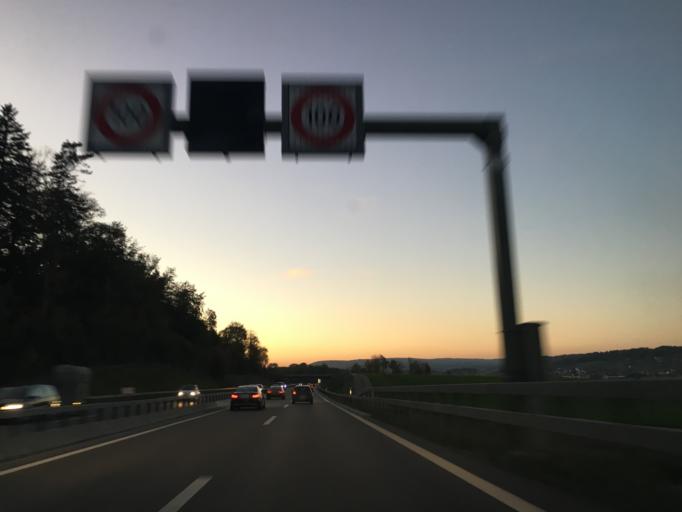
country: CH
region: Zurich
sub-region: Bezirk Andelfingen
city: Marthalen
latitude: 47.6332
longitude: 8.6664
